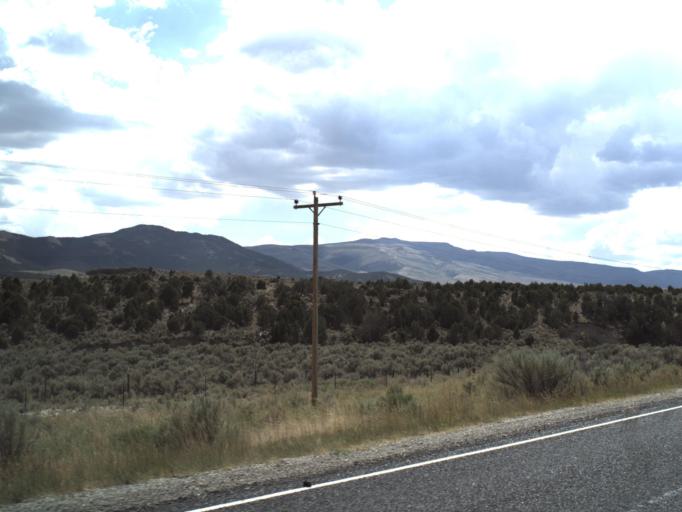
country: US
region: Idaho
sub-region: Minidoka County
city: Rupert
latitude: 41.9718
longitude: -113.1444
